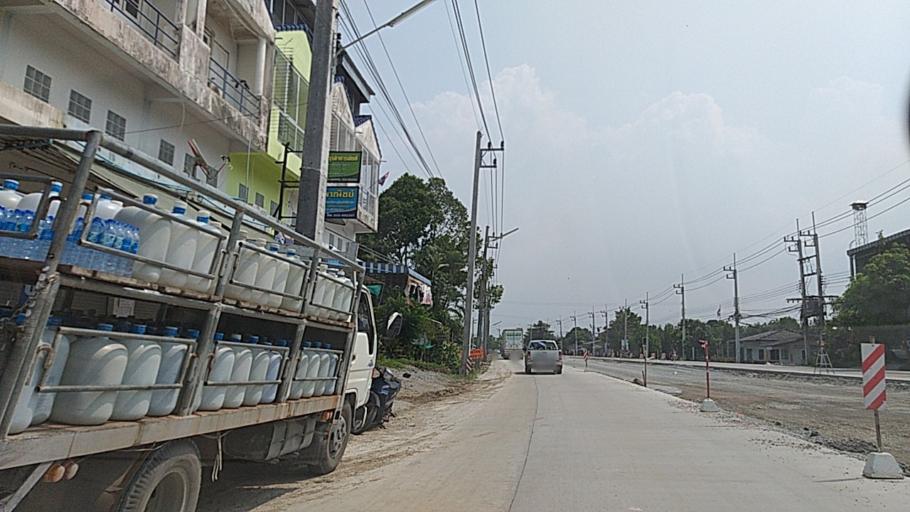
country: TH
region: Chon Buri
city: Phanat Nikhom
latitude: 13.3984
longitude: 101.1904
